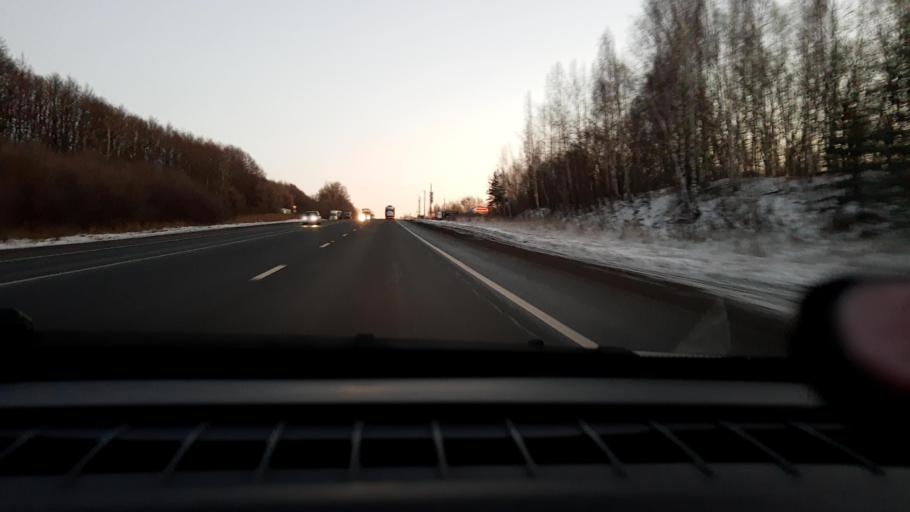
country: RU
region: Nizjnij Novgorod
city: Pervoye Maya
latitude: 55.9955
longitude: 44.7544
